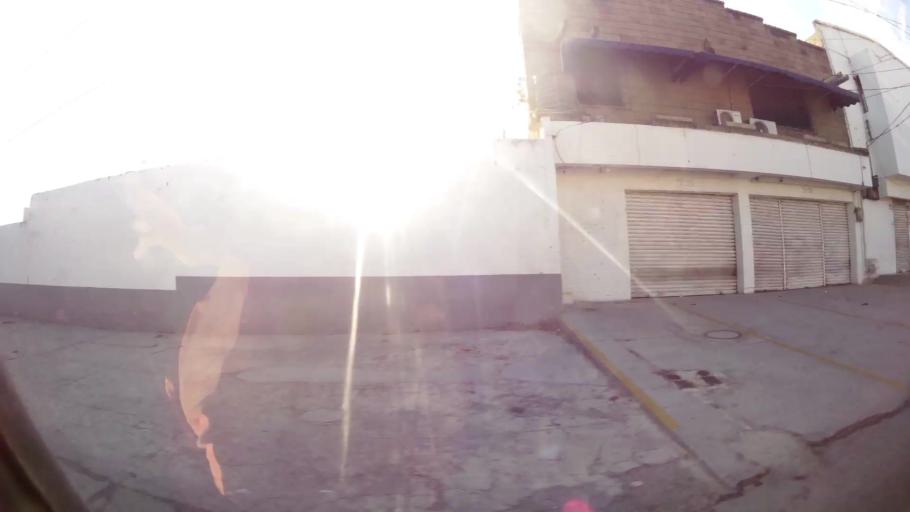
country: CO
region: Atlantico
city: Barranquilla
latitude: 11.0136
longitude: -74.7972
